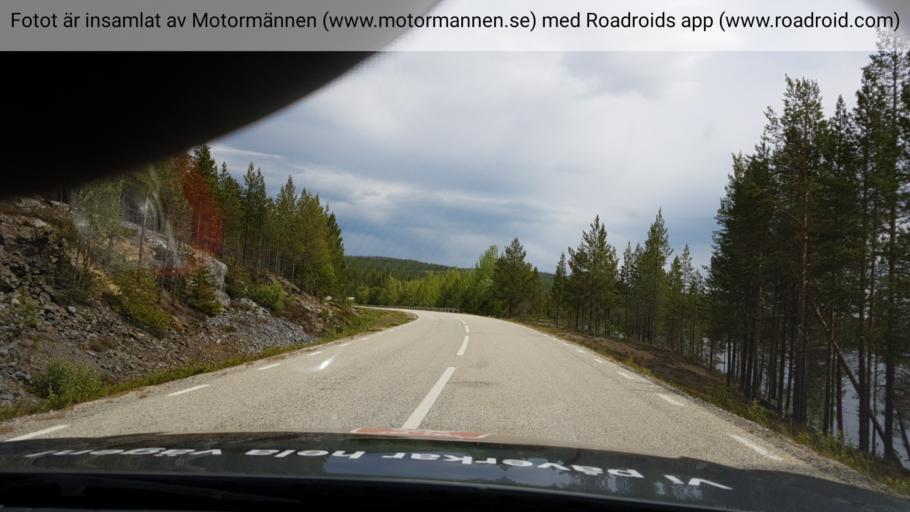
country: SE
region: Jaemtland
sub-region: Are Kommun
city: Jarpen
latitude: 62.8253
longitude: 13.4793
